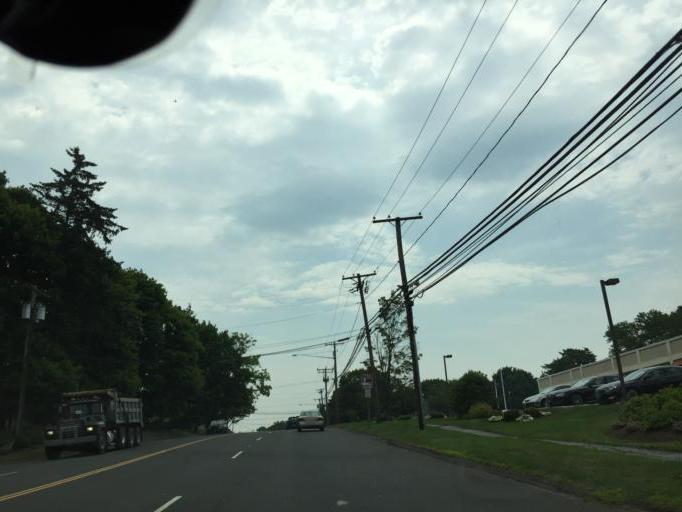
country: US
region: Connecticut
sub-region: Fairfield County
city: Westport
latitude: 41.1382
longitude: -73.3436
